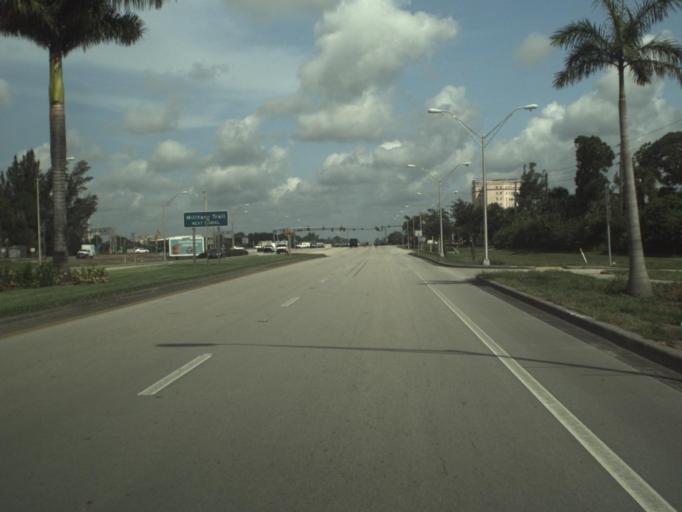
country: US
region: Florida
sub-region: Palm Beach County
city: Mangonia Park
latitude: 26.7780
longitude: -80.1045
